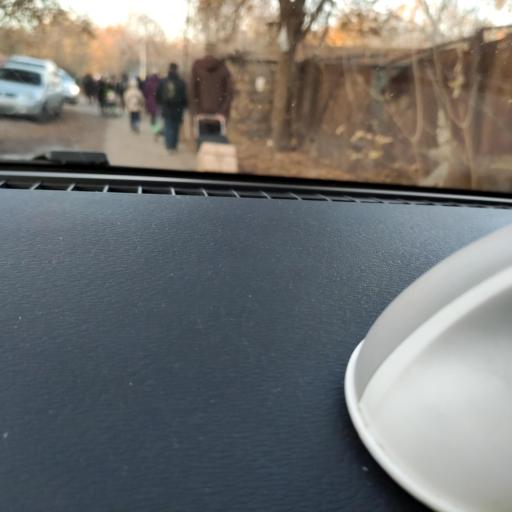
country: RU
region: Samara
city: Samara
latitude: 53.2007
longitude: 50.2393
